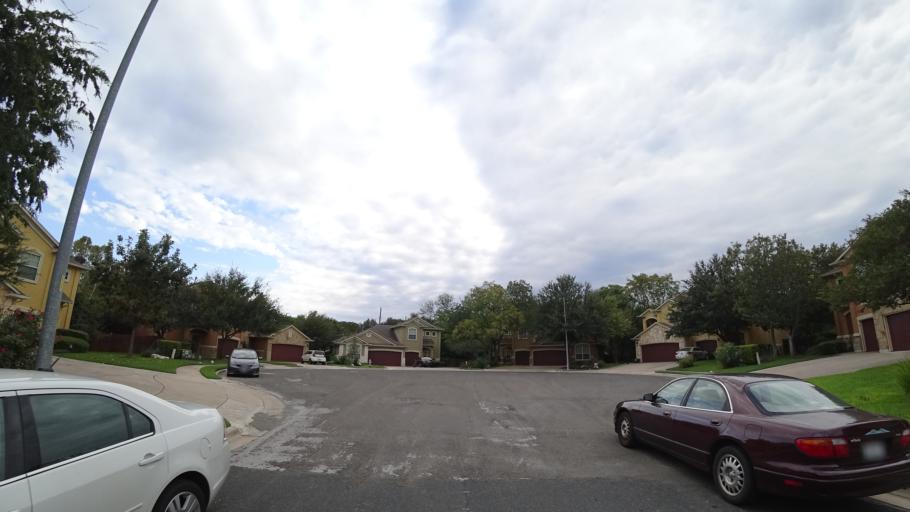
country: US
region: Texas
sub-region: Travis County
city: Rollingwood
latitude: 30.2196
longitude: -97.7932
